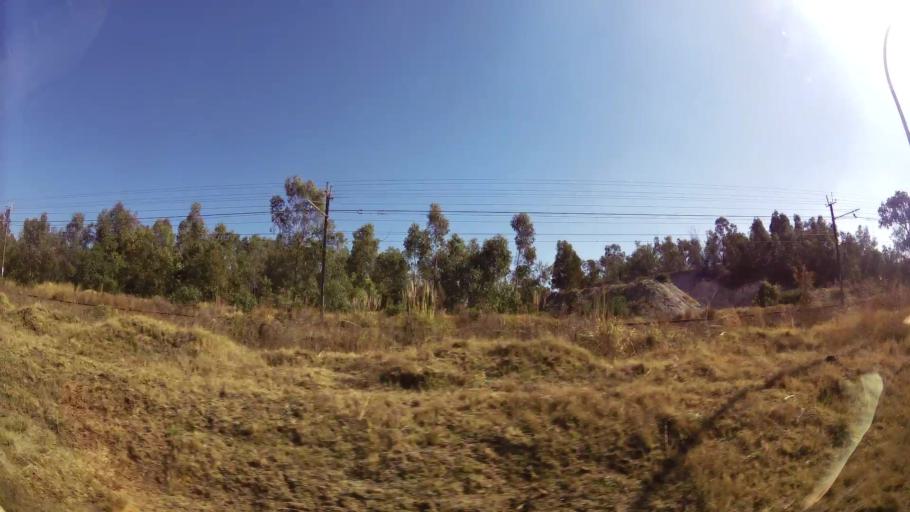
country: ZA
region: Mpumalanga
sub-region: Nkangala District Municipality
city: Witbank
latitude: -25.8307
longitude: 29.2400
